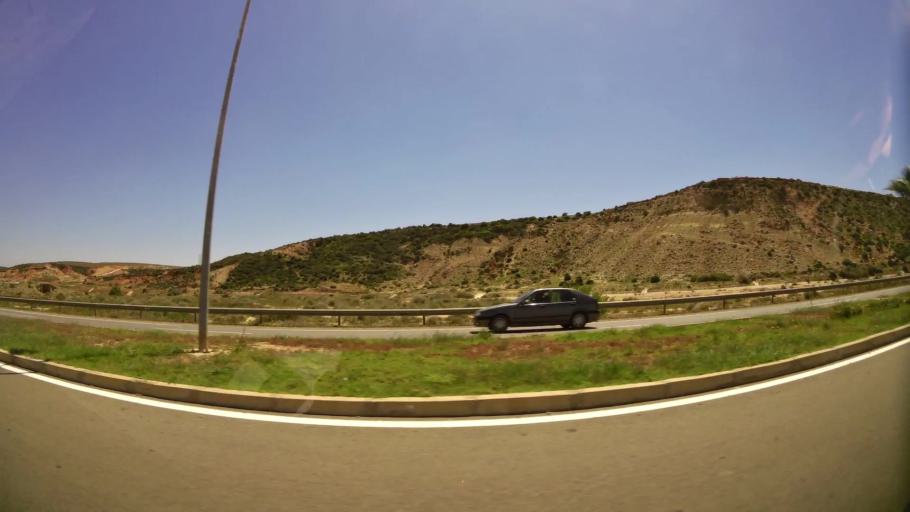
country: MA
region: Oriental
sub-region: Berkane-Taourirt
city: Madagh
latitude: 35.0945
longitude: -2.3153
